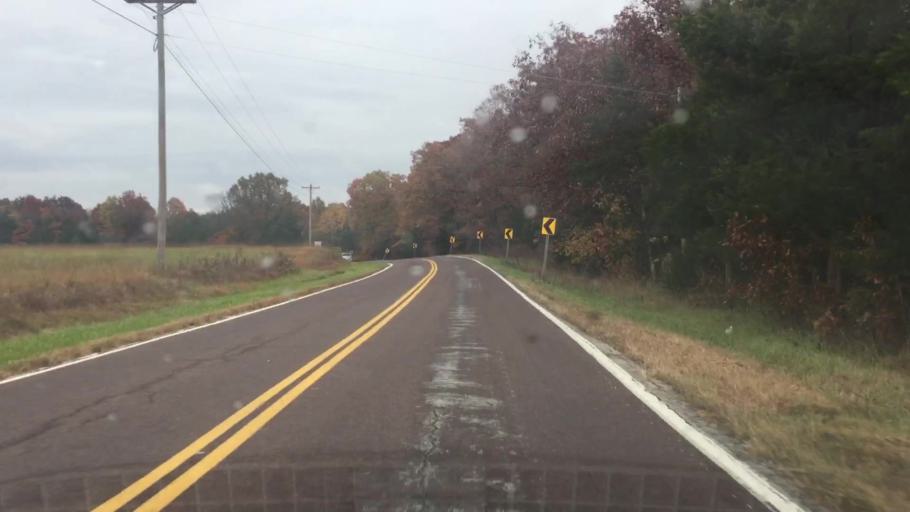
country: US
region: Missouri
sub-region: Callaway County
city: Fulton
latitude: 38.7826
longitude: -91.8158
